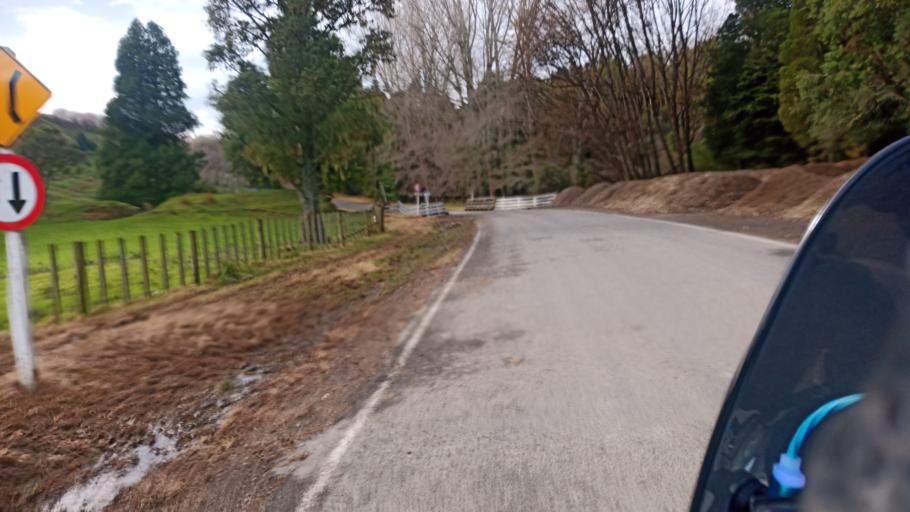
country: NZ
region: Gisborne
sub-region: Gisborne District
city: Gisborne
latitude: -38.4160
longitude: 177.9248
